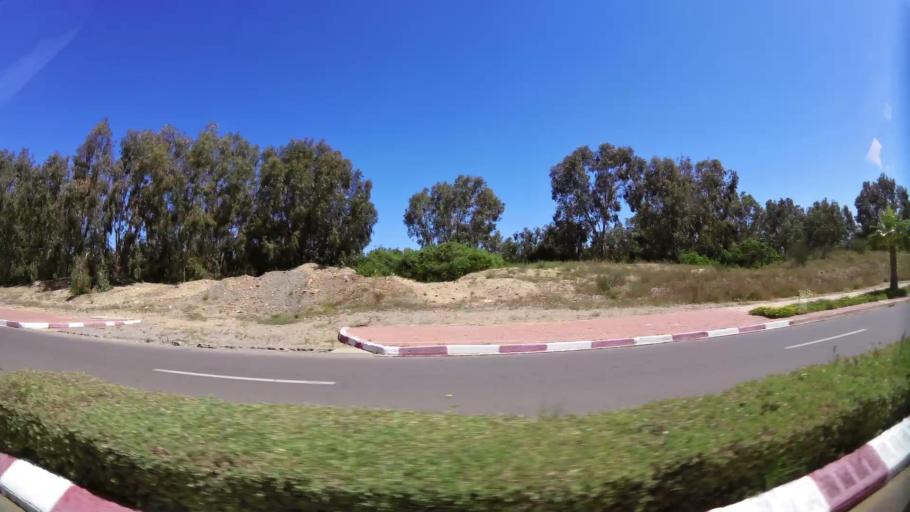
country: MA
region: Oriental
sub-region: Berkane-Taourirt
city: Madagh
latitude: 35.0943
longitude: -2.2683
